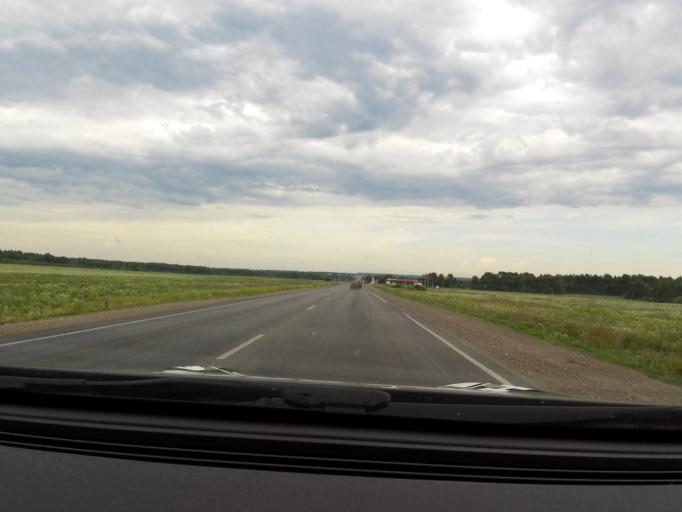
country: RU
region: Bashkortostan
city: Kudeyevskiy
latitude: 54.8173
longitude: 56.8116
